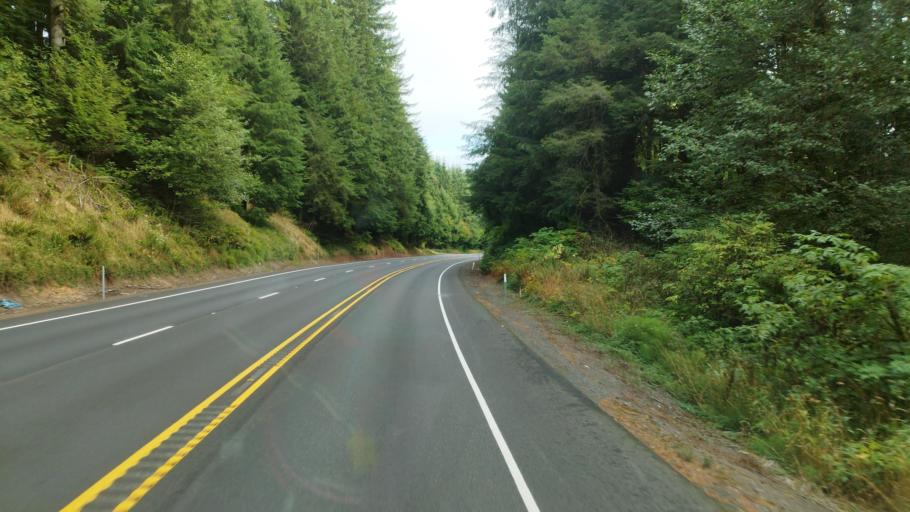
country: US
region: Oregon
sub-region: Clatsop County
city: Seaside
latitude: 45.9019
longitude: -123.6703
